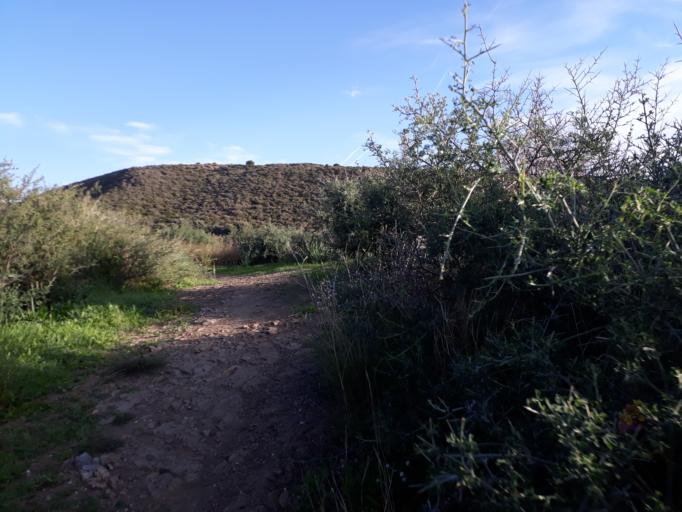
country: ES
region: Andalusia
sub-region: Provincia de Malaga
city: Fuengirola
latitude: 36.5062
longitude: -4.6980
